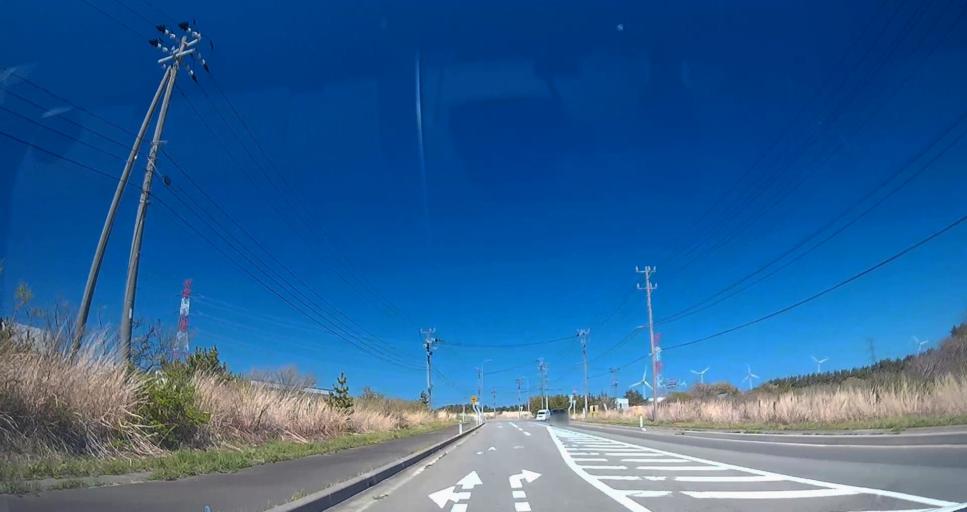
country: JP
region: Hokkaido
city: Hakodate
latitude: 41.5082
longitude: 140.9177
